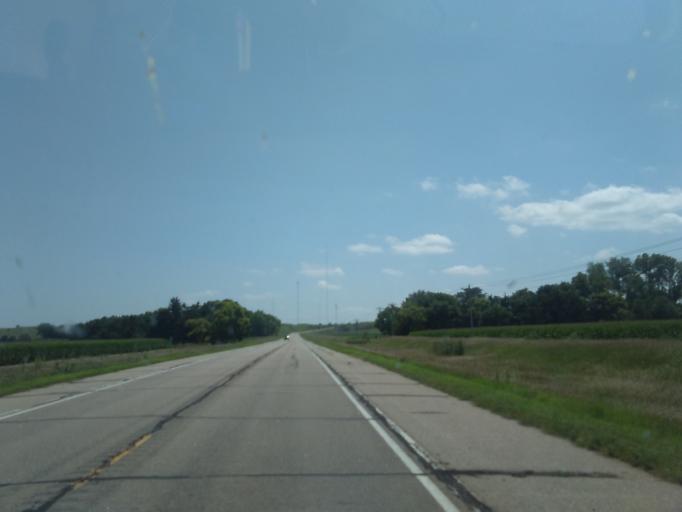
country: US
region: Nebraska
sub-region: Dawson County
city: Lexington
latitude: 40.7163
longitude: -99.7874
